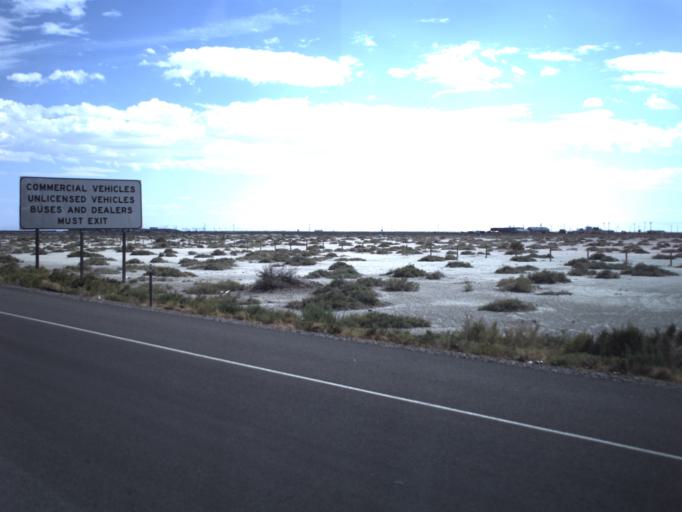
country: US
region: Utah
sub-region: Tooele County
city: Wendover
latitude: 40.7470
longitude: -114.0098
